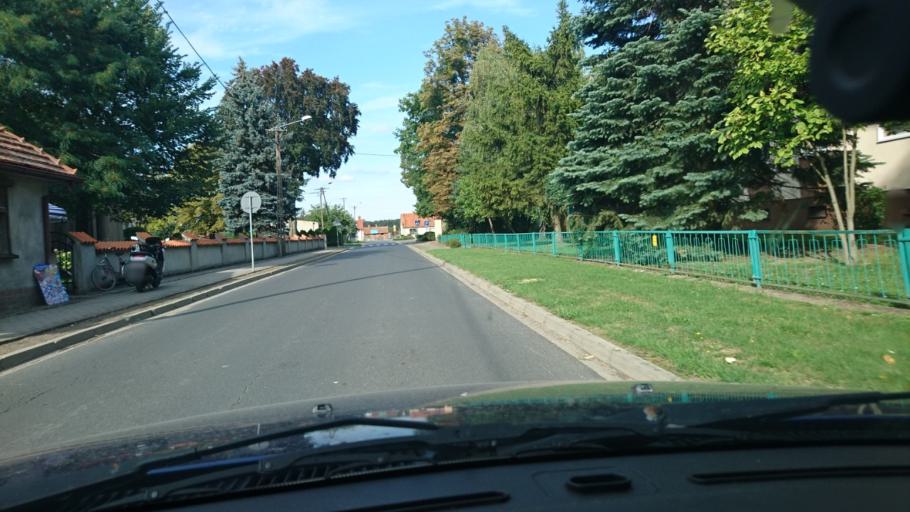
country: PL
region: Greater Poland Voivodeship
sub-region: Powiat rawicki
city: Jutrosin
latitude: 51.7002
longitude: 17.1735
